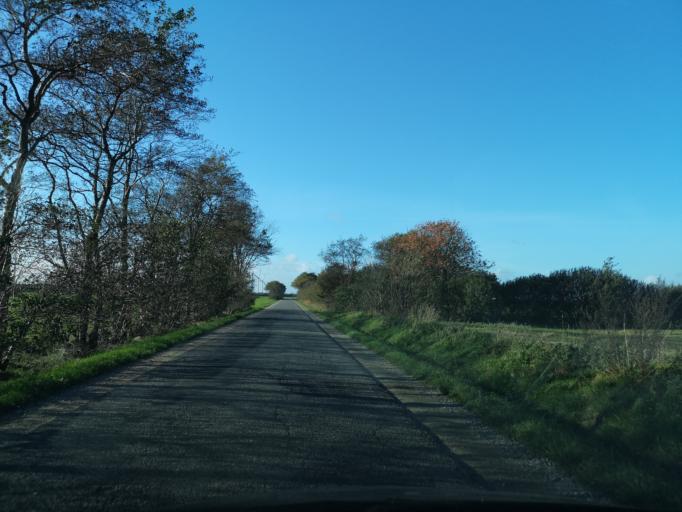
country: DK
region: Central Jutland
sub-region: Ringkobing-Skjern Kommune
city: Tarm
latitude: 55.8053
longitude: 8.4497
